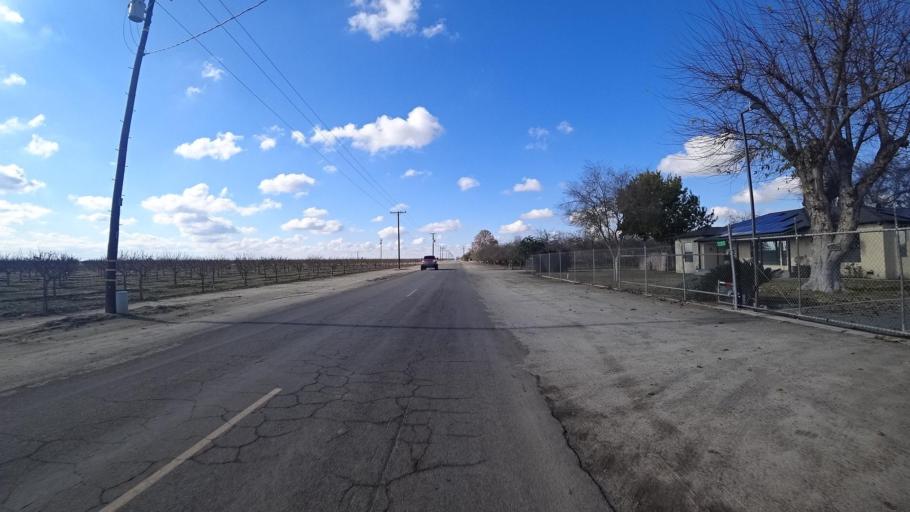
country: US
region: California
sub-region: Kern County
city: Delano
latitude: 35.7323
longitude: -119.2608
